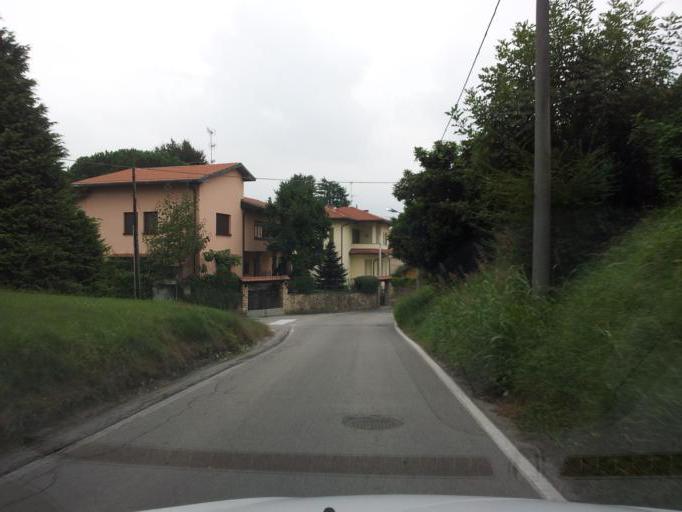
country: IT
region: Lombardy
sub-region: Provincia di Varese
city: Sesto Calende
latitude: 45.7302
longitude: 8.6399
